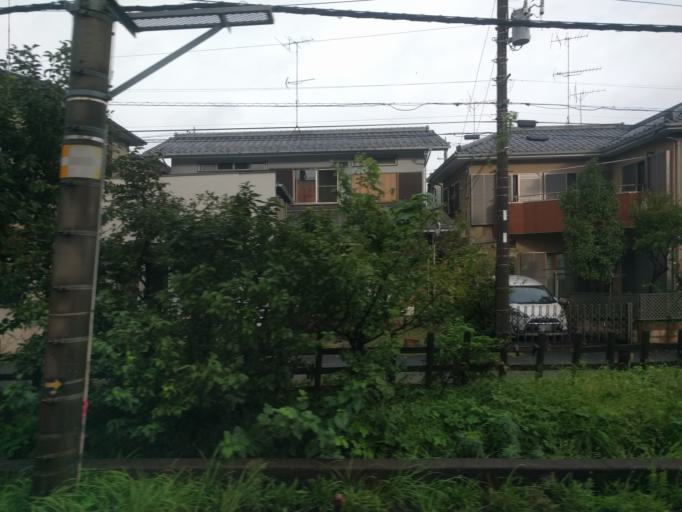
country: JP
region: Tokyo
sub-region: Machida-shi
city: Machida
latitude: 35.5343
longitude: 139.5027
